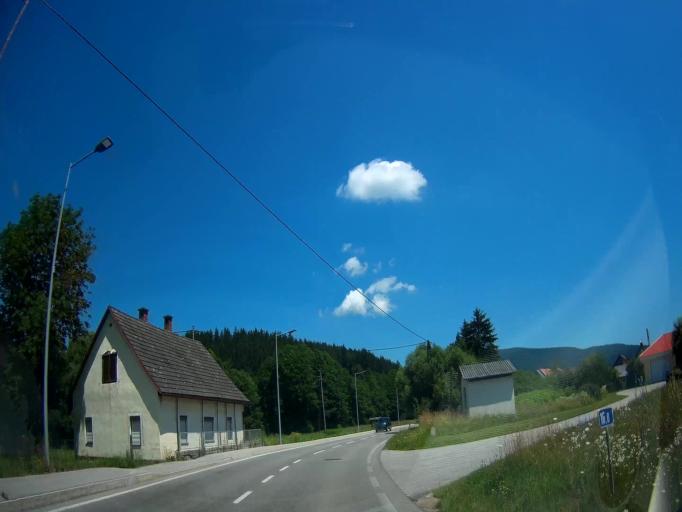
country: AT
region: Carinthia
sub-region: Politischer Bezirk Volkermarkt
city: Bleiburg/Pliberk
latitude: 46.5764
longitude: 14.7806
